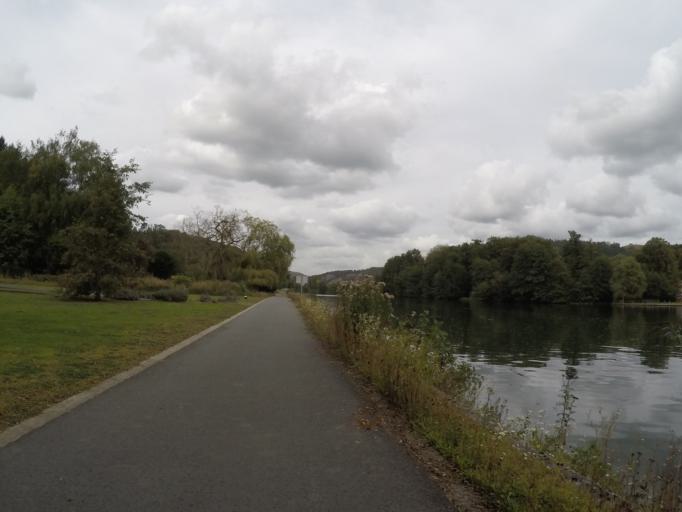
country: BE
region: Wallonia
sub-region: Province de Namur
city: Yvoir
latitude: 50.3209
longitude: 4.8748
